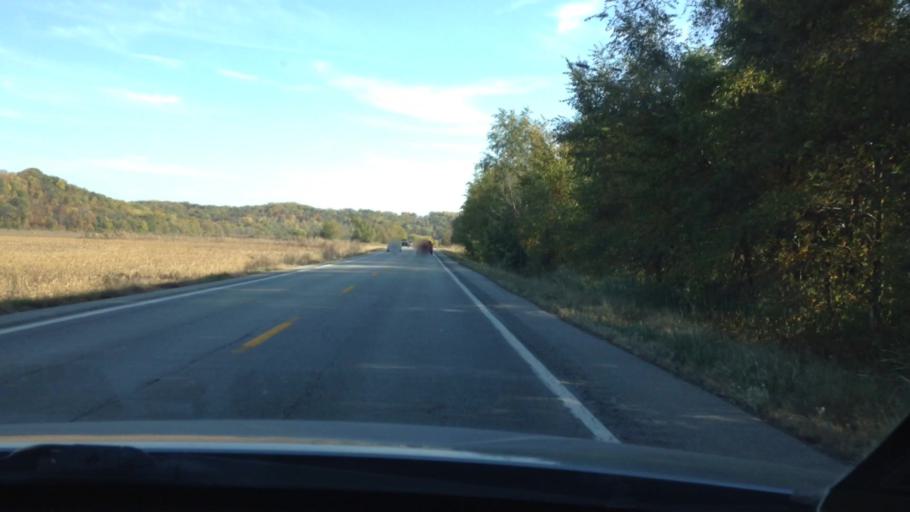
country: US
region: Kansas
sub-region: Leavenworth County
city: Lansing
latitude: 39.2644
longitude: -94.8162
